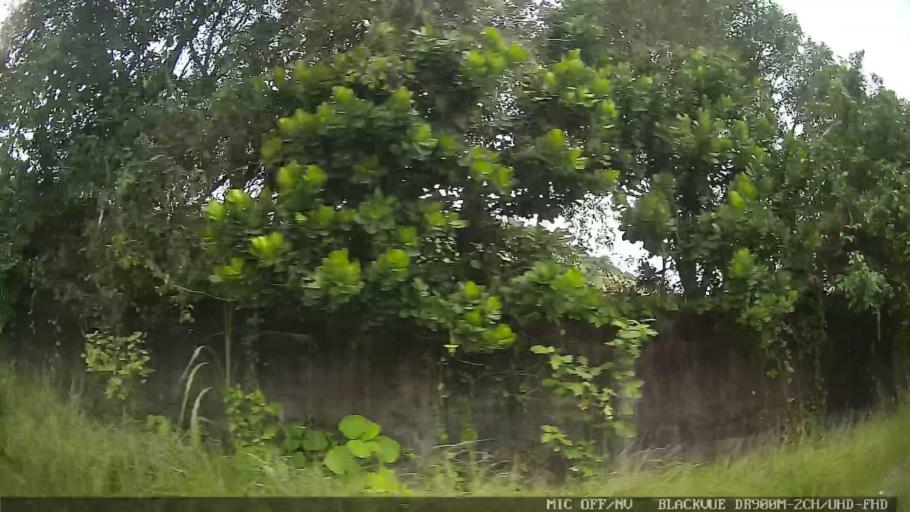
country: BR
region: Sao Paulo
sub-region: Guaruja
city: Guaruja
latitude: -24.0149
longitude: -46.2794
